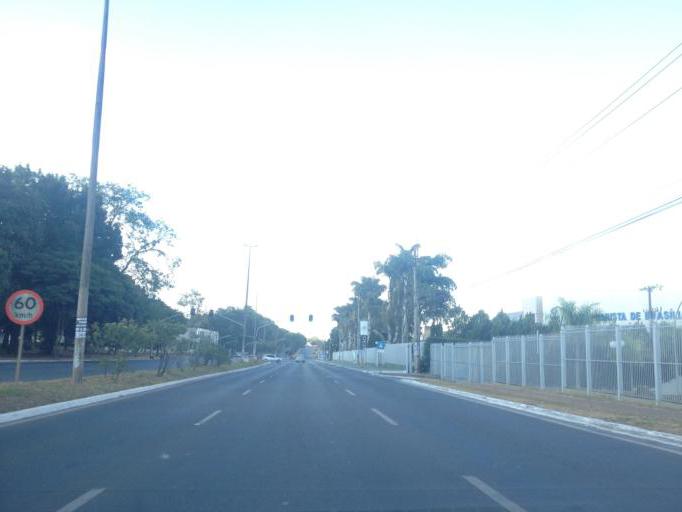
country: BR
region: Federal District
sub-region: Brasilia
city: Brasilia
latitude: -15.8373
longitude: -47.9177
